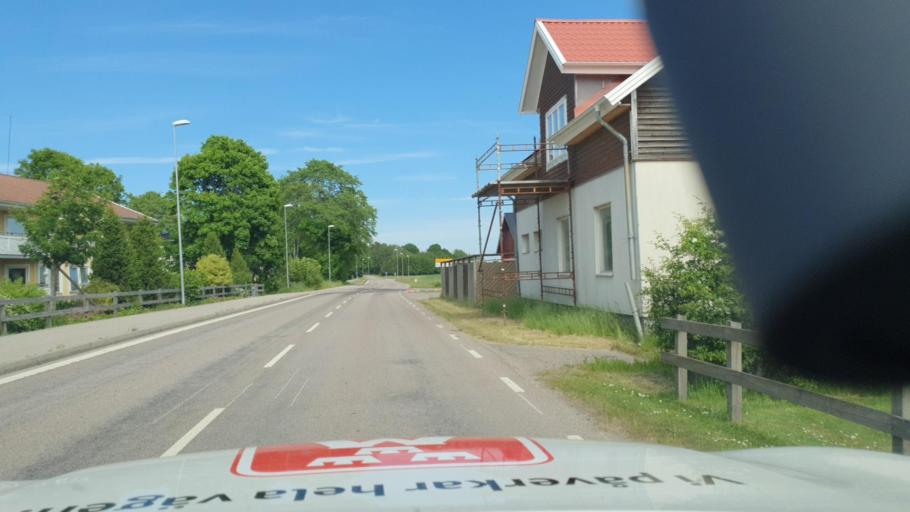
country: SE
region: Vaestra Goetaland
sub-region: Essunga Kommun
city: Nossebro
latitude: 58.2314
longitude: 12.6635
